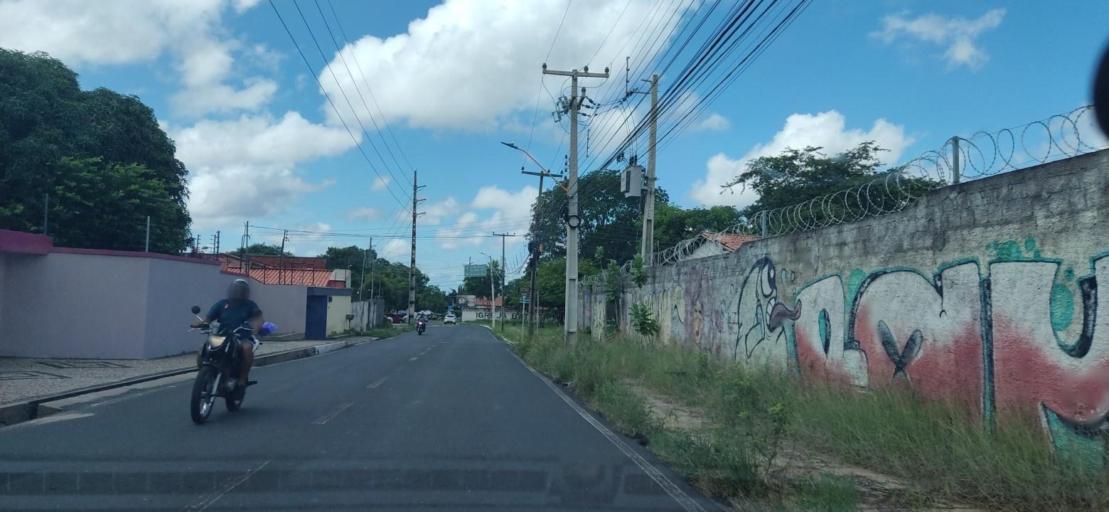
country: BR
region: Piaui
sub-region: Teresina
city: Teresina
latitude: -5.0691
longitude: -42.7604
